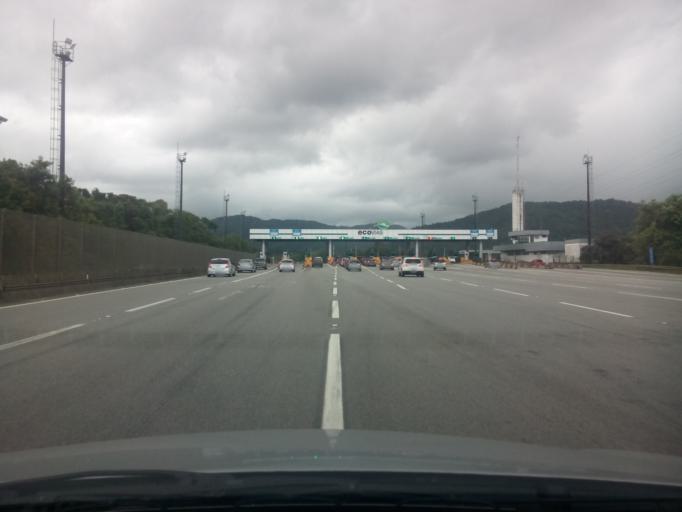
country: BR
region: Sao Paulo
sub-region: Santos
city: Santos
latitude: -23.8960
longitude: -46.3017
